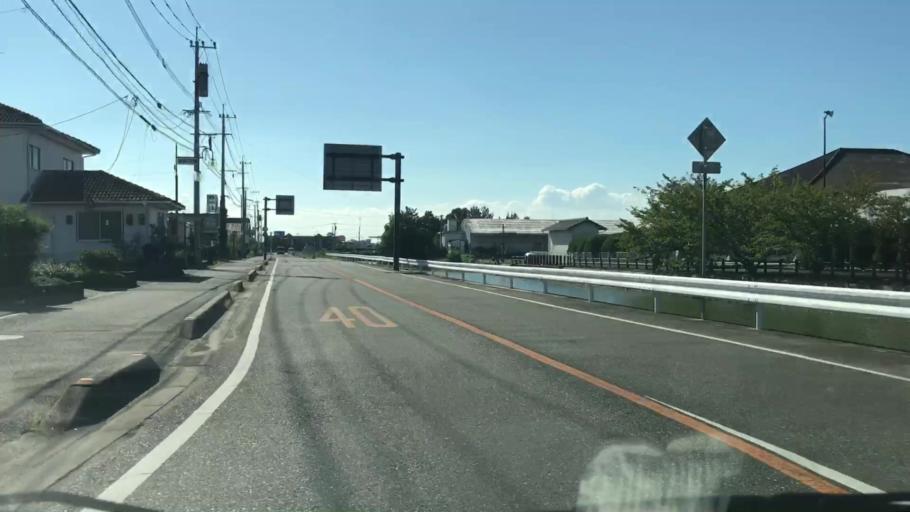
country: JP
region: Saga Prefecture
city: Okawa
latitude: 33.1915
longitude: 130.3192
